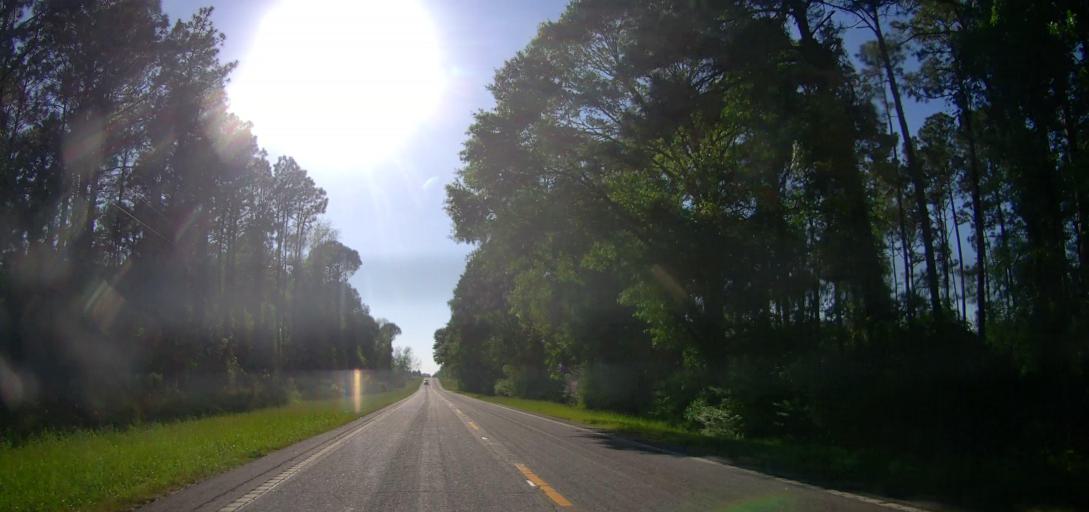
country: US
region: Georgia
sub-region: Ben Hill County
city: Fitzgerald
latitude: 31.7187
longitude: -83.3454
